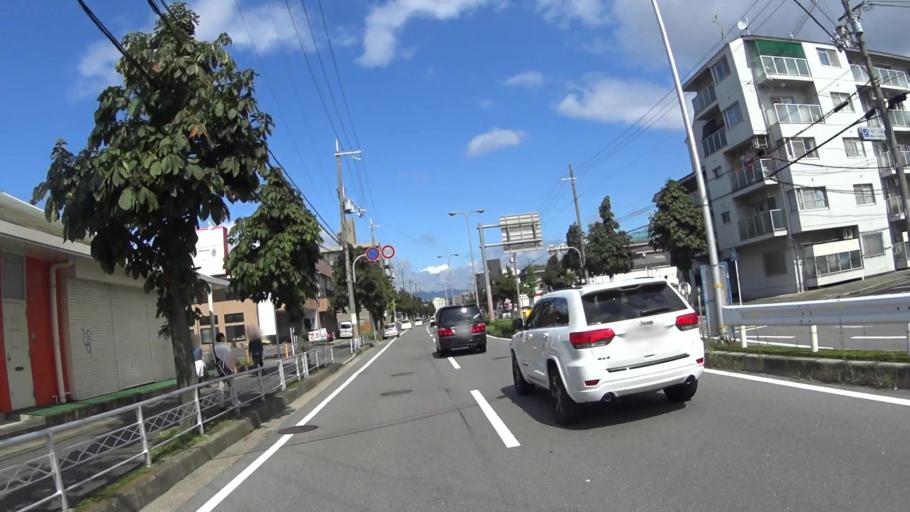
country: JP
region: Kyoto
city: Muko
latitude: 34.9742
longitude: 135.7142
